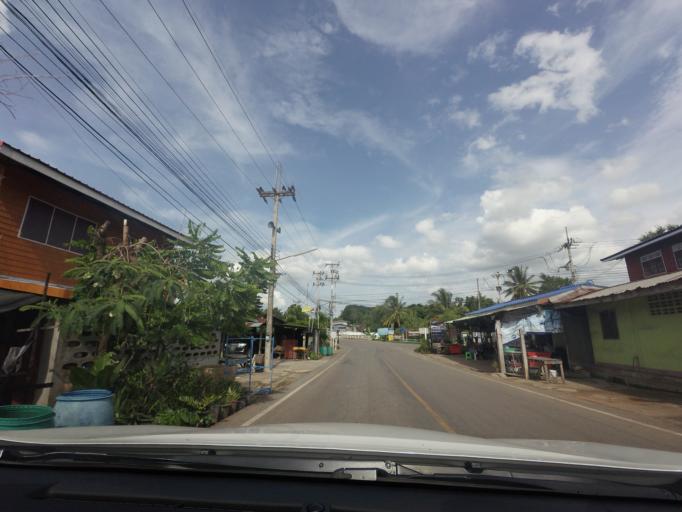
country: TH
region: Nakhon Ratchasima
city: Pak Chong
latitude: 14.5243
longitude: 101.4766
